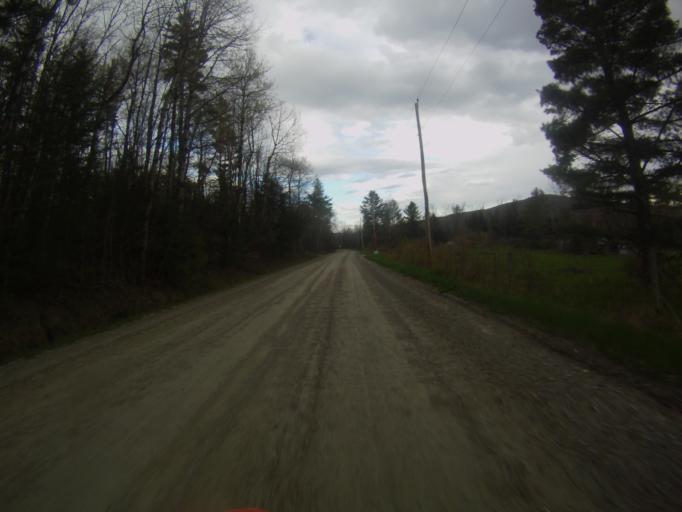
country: US
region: Vermont
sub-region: Addison County
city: Bristol
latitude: 44.0381
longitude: -73.0158
